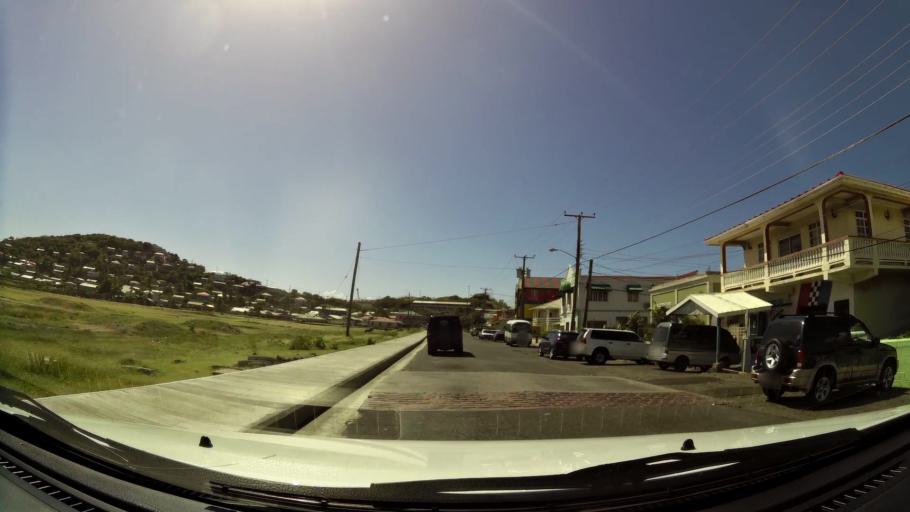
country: LC
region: Vieux-Fort
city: Vieux Fort
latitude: 13.7277
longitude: -60.9520
